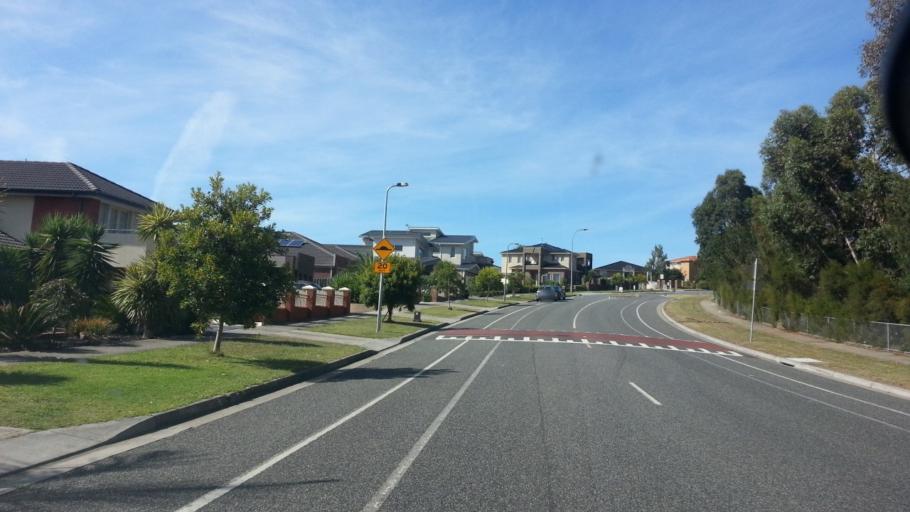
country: AU
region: Victoria
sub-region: Casey
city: Endeavour Hills
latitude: -37.9733
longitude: 145.2776
